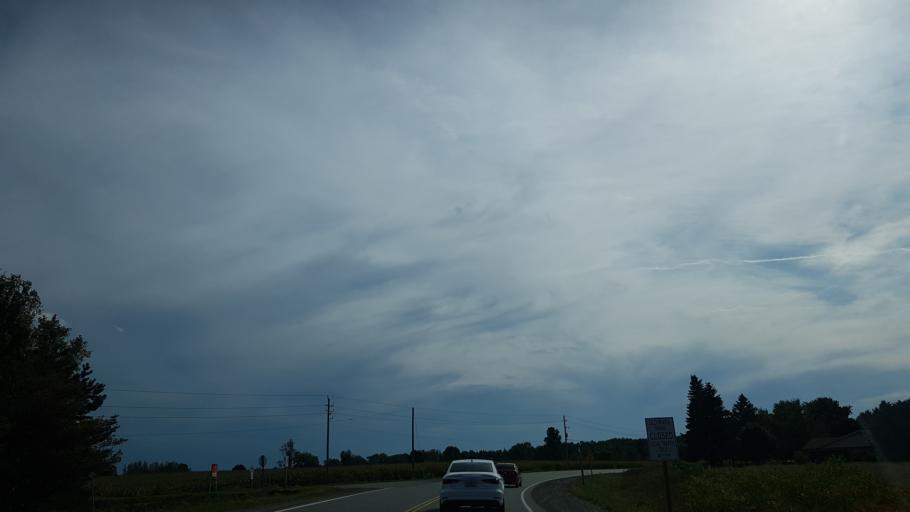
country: CA
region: Ontario
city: Delaware
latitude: 42.9795
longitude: -81.3860
